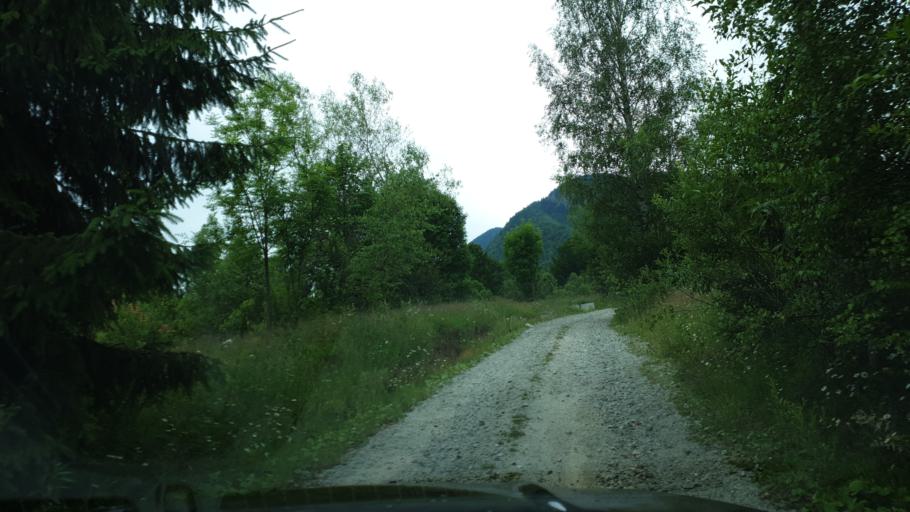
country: RO
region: Hunedoara
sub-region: Comuna Uricani
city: Uricani
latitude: 45.3058
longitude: 22.9848
